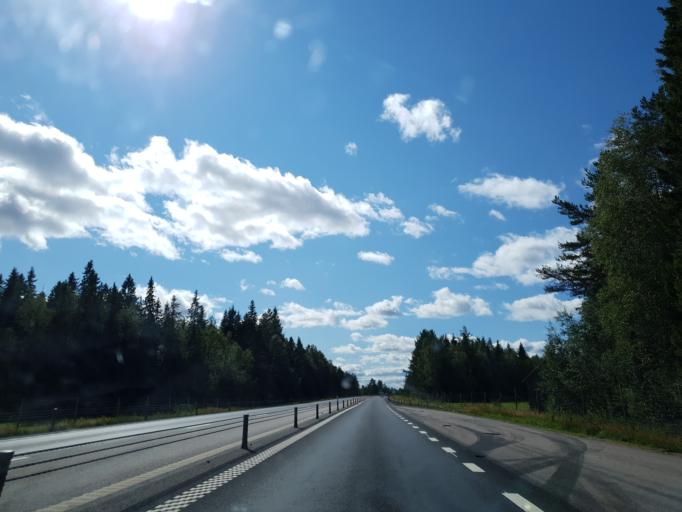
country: SE
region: Vaesterbotten
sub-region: Nordmalings Kommun
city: Nordmaling
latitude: 63.5309
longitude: 19.3952
